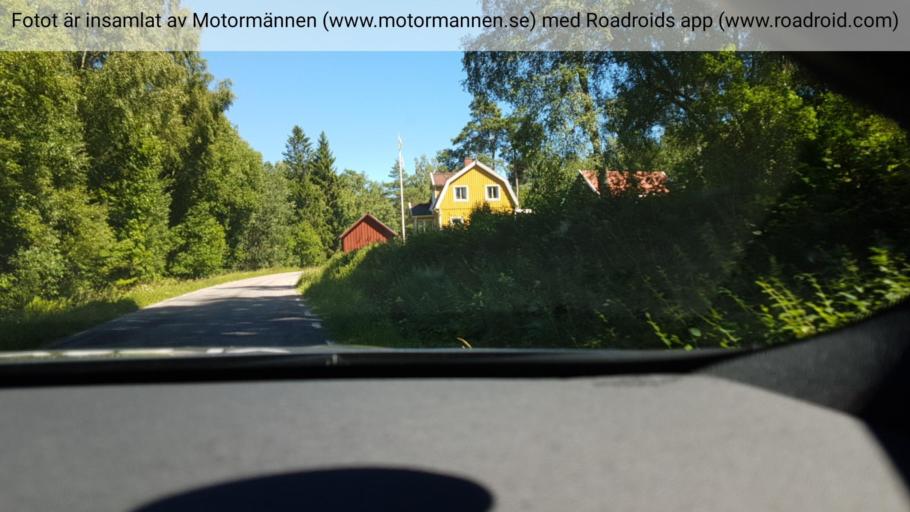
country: SE
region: Vaestra Goetaland
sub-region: Falkopings Kommun
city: Falkoeping
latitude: 58.0701
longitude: 13.4728
